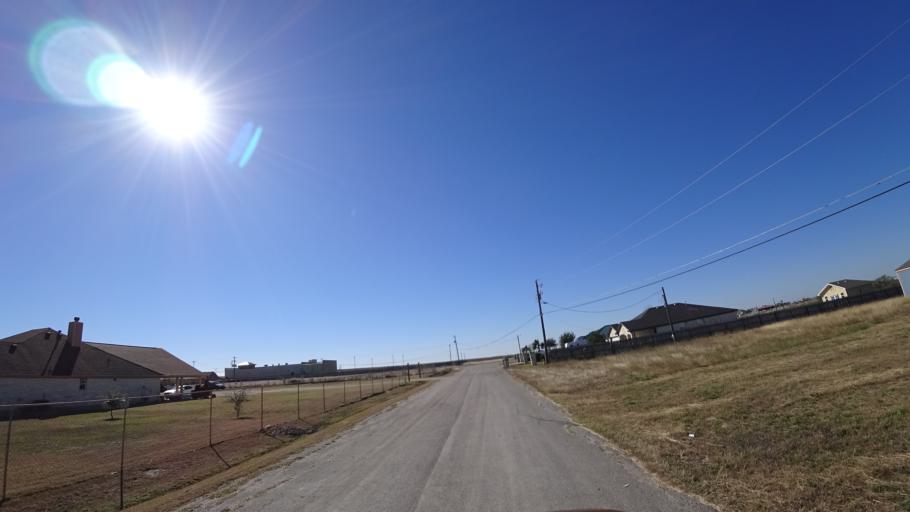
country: US
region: Texas
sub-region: Travis County
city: Garfield
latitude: 30.1032
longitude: -97.6066
